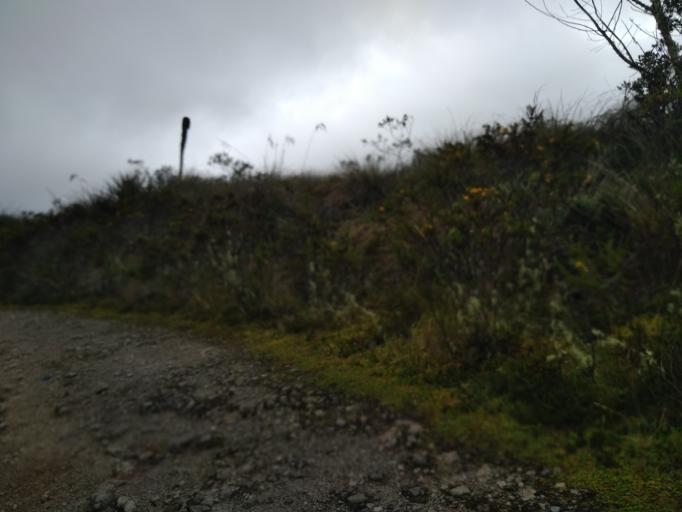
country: EC
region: Carchi
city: San Gabriel
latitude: 0.6887
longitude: -77.8502
